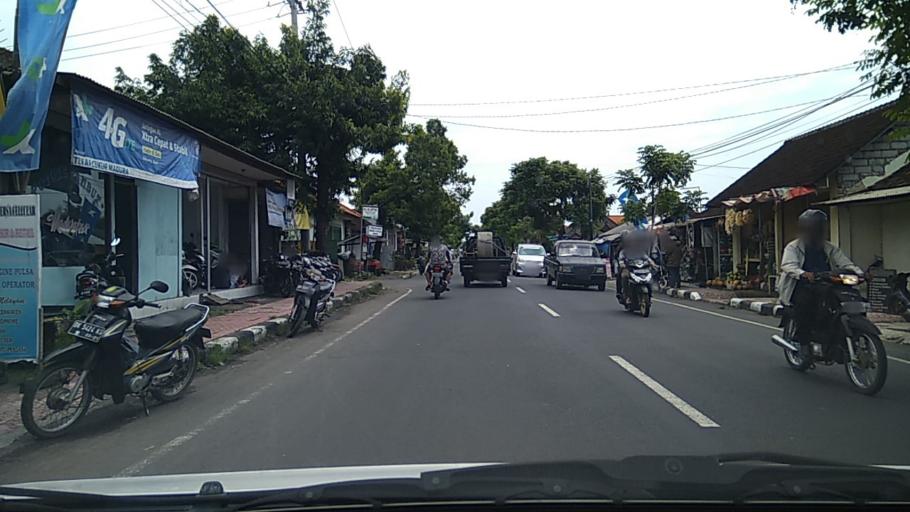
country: ID
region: Bali
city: Banjar Pesalakan
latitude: -8.5349
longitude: 115.3144
